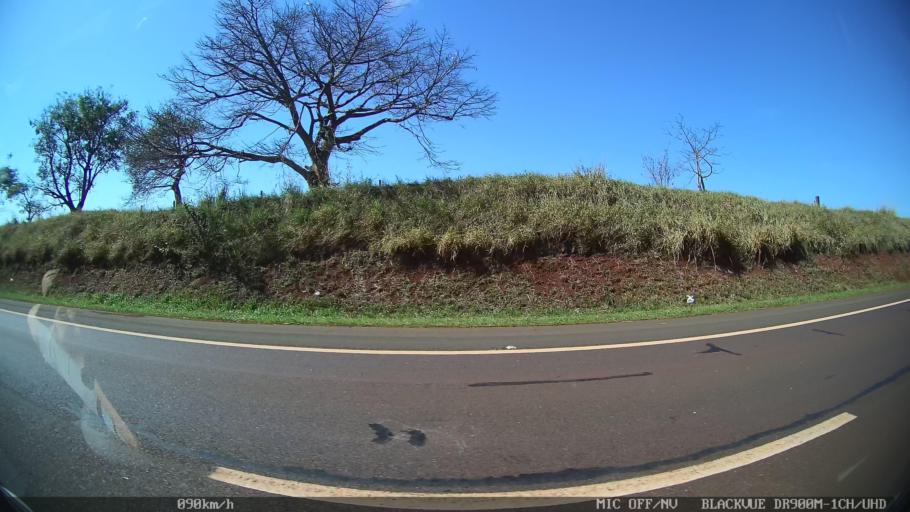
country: BR
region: Sao Paulo
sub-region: Batatais
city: Batatais
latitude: -20.7611
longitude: -47.5326
